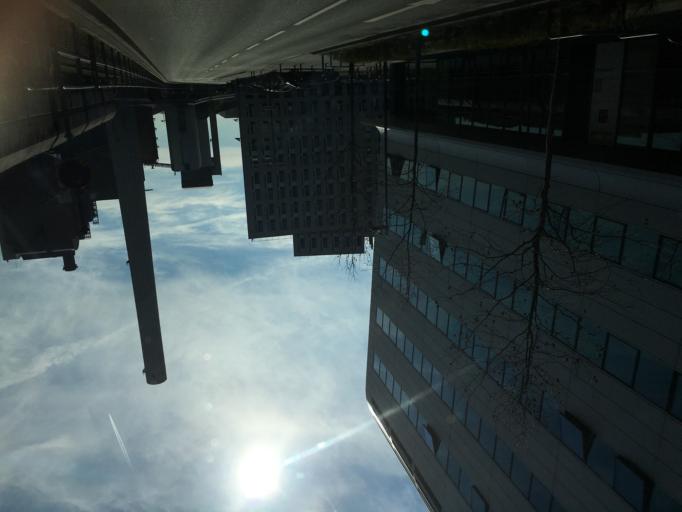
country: DE
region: Hesse
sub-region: Regierungsbezirk Darmstadt
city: Frankfurt am Main
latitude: 50.0998
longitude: 8.6588
